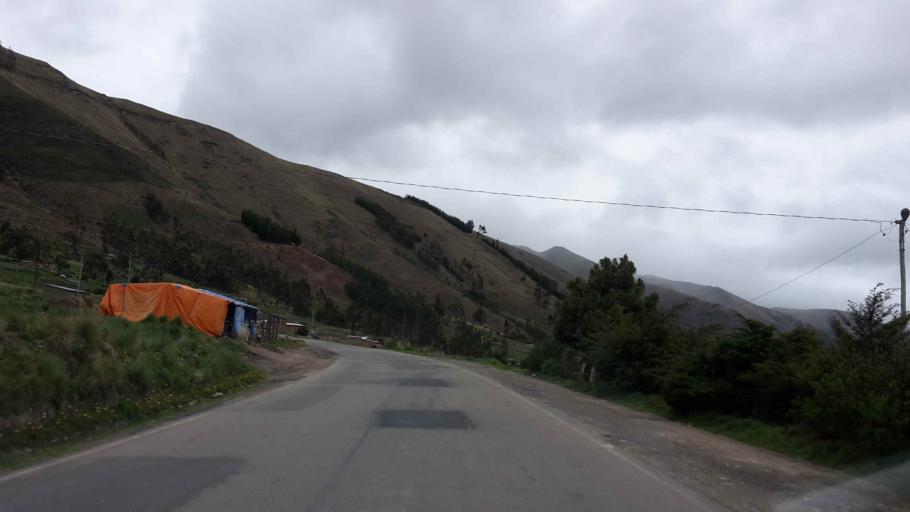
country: BO
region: Cochabamba
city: Arani
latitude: -17.4829
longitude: -65.5470
